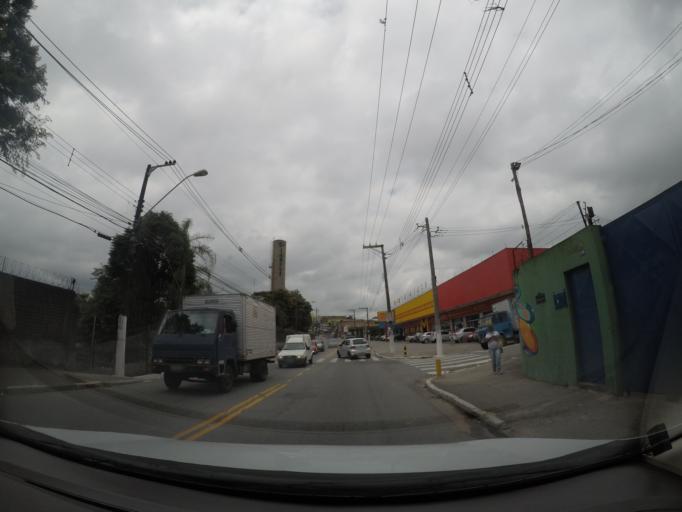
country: BR
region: Sao Paulo
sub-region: Itaquaquecetuba
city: Itaquaquecetuba
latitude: -23.4555
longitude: -46.4080
